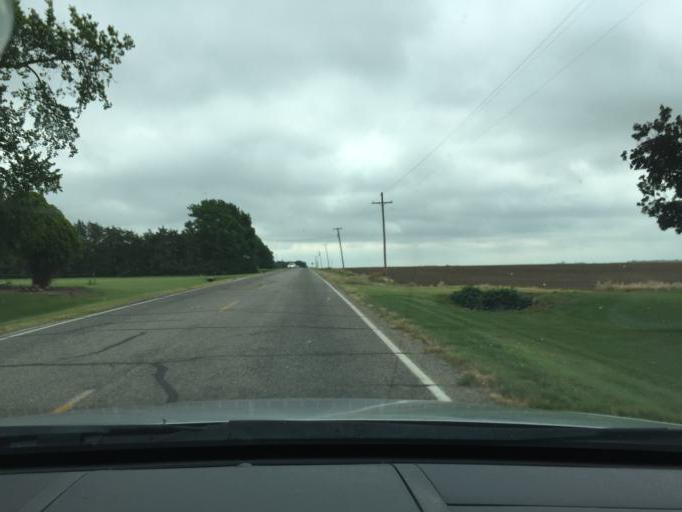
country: US
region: Kansas
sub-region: Reno County
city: South Hutchinson
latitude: 37.9700
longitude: -98.0198
